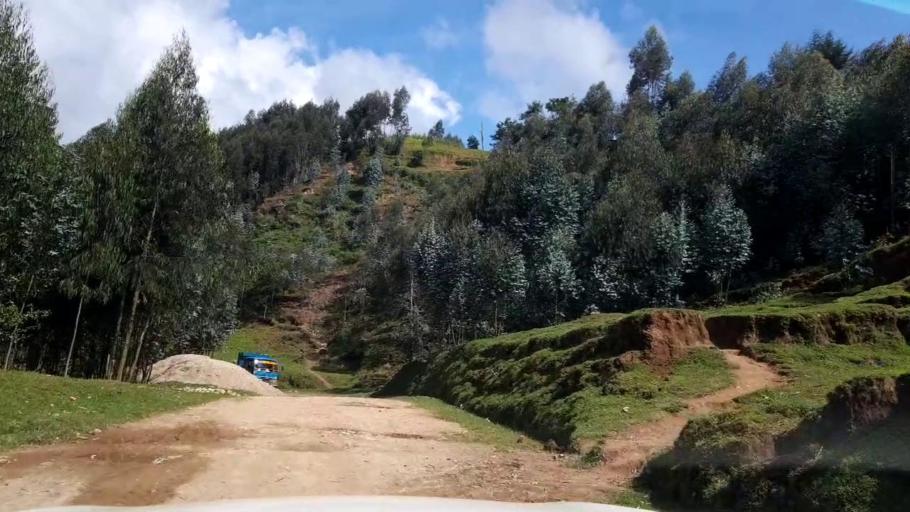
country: RW
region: Western Province
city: Kibuye
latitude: -1.8872
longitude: 29.4676
